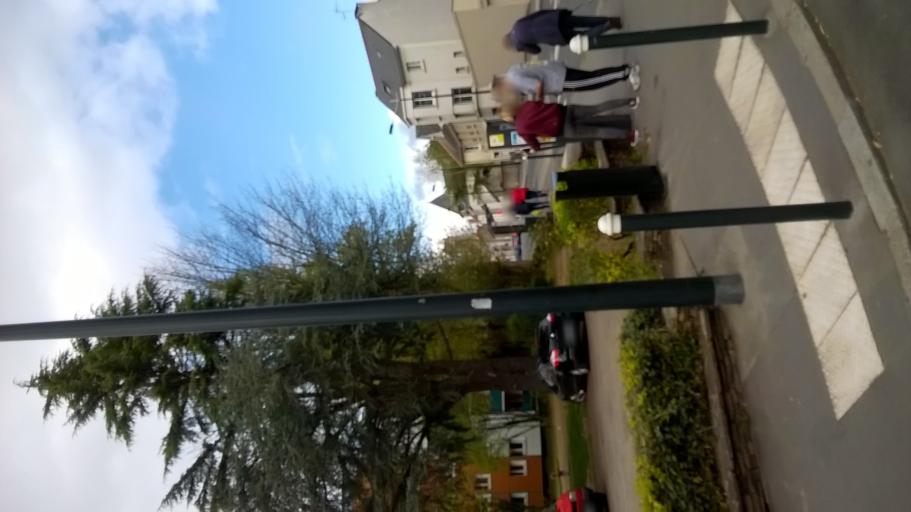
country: FR
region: Pays de la Loire
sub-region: Departement de la Loire-Atlantique
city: Nantes
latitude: 47.2266
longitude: -1.5468
